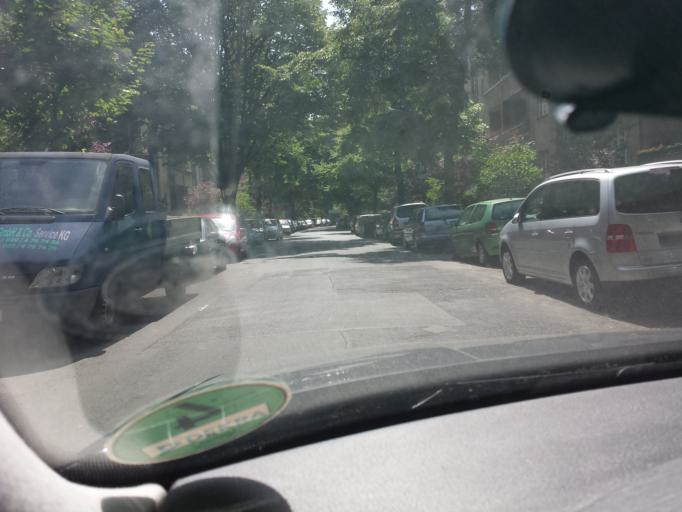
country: DE
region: Berlin
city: Pankow
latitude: 52.5632
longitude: 13.3938
